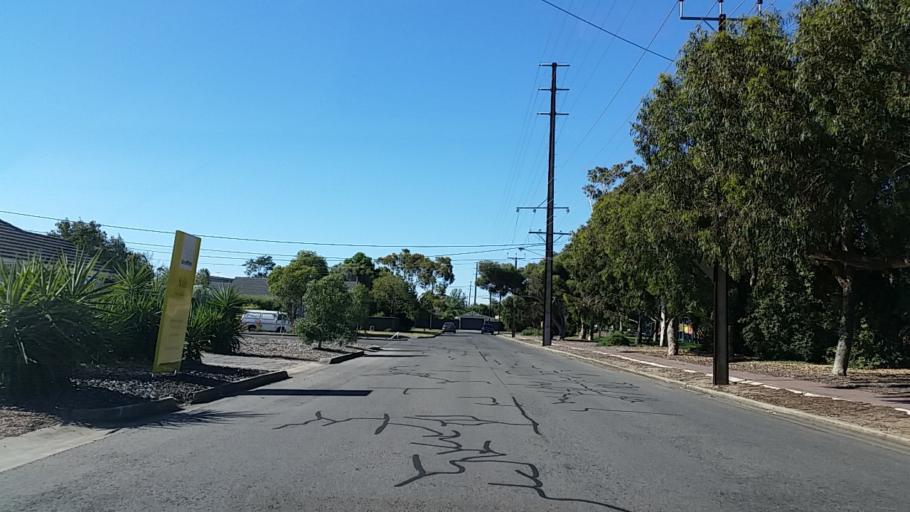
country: AU
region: South Australia
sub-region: Charles Sturt
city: Henley Beach
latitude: -34.9238
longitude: 138.5064
